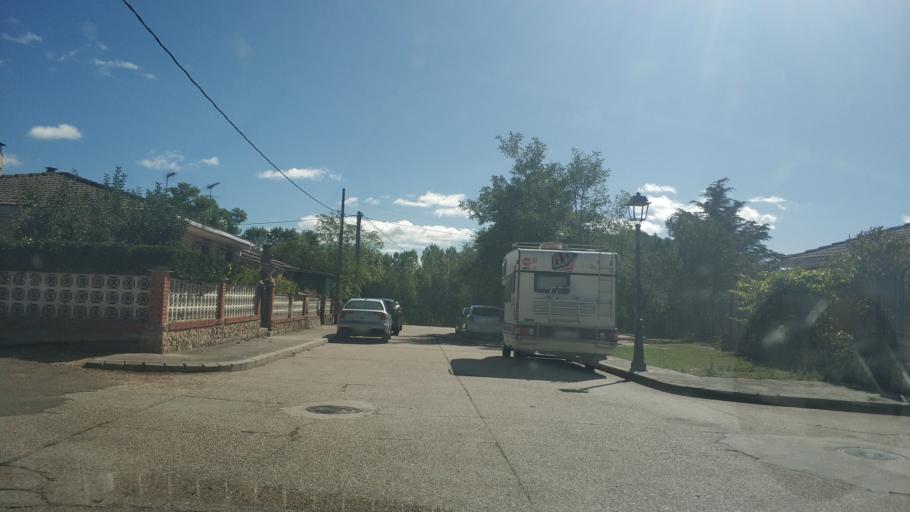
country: ES
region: Castille and Leon
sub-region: Provincia de Burgos
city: Santa Ines
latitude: 42.0315
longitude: -3.6467
